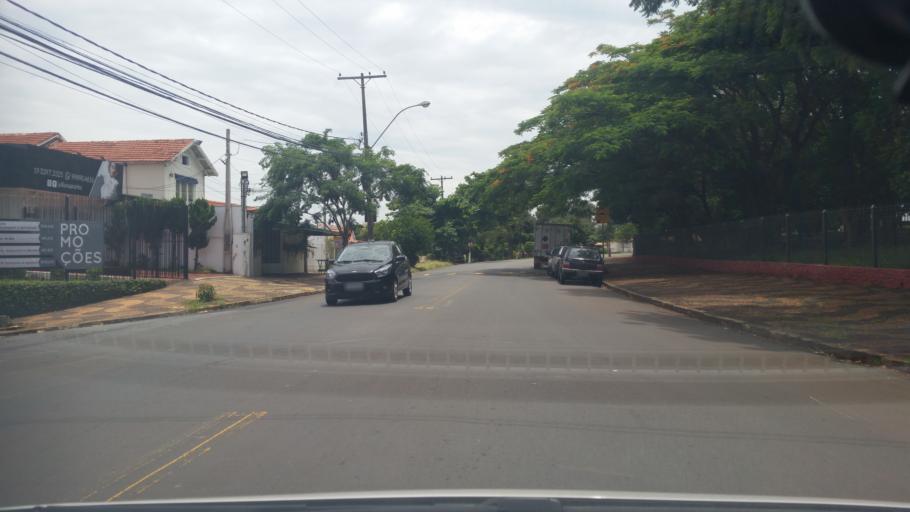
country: BR
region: Sao Paulo
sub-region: Campinas
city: Campinas
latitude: -22.8746
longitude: -47.0638
